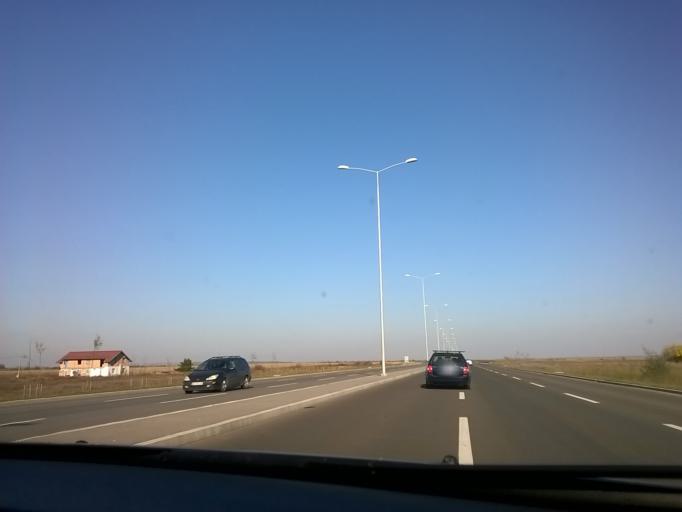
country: RS
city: Ovca
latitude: 44.8879
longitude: 20.5179
